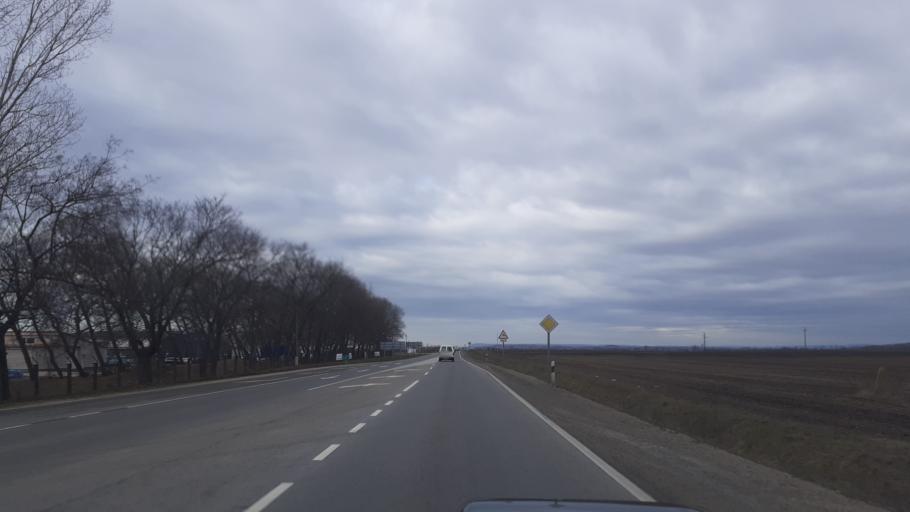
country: HU
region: Fejer
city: Seregelyes
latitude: 47.1439
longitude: 18.5303
